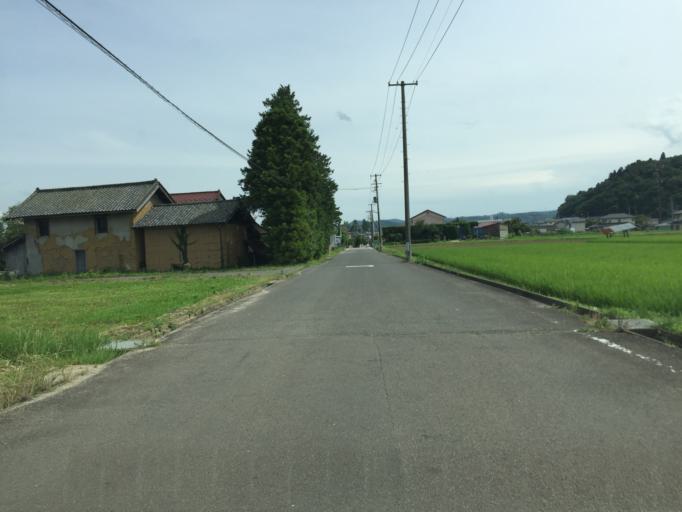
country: JP
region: Fukushima
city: Fukushima-shi
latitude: 37.7325
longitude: 140.4369
